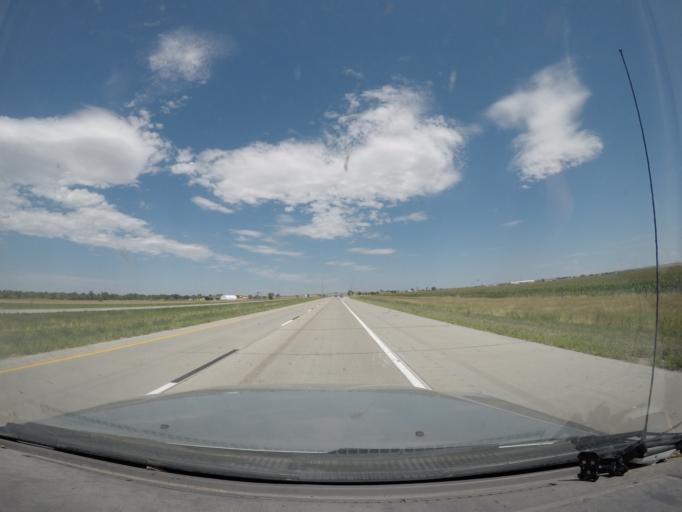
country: US
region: Colorado
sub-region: Sedgwick County
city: Julesburg
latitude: 41.0460
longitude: -102.0795
